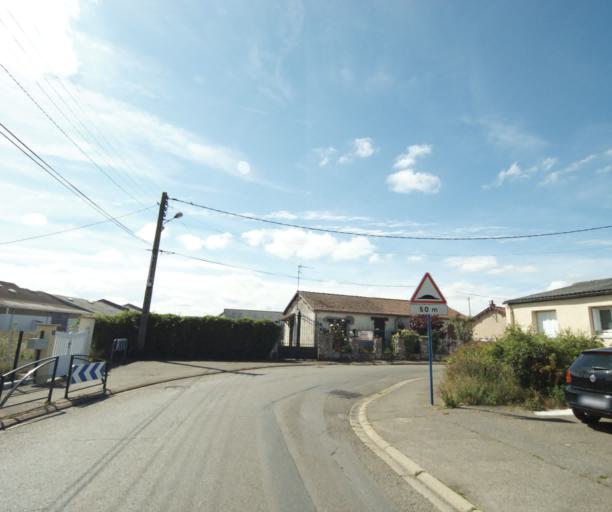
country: FR
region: Centre
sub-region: Departement d'Eure-et-Loir
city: Luce
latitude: 48.4306
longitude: 1.4534
